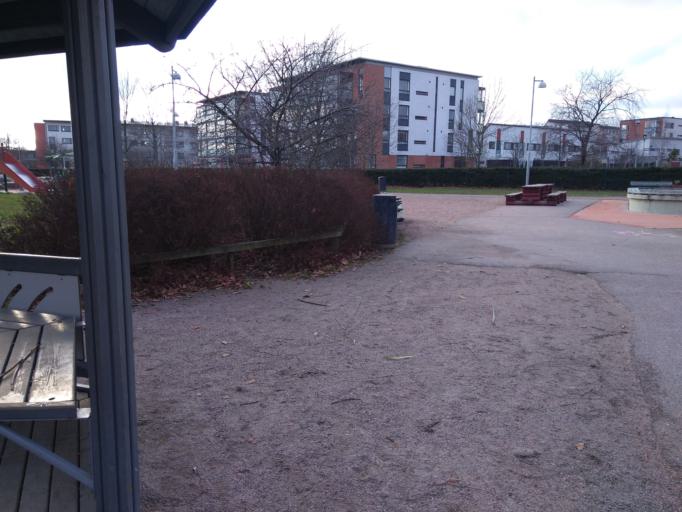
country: FI
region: Uusimaa
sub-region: Helsinki
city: Vantaa
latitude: 60.2299
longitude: 25.0335
